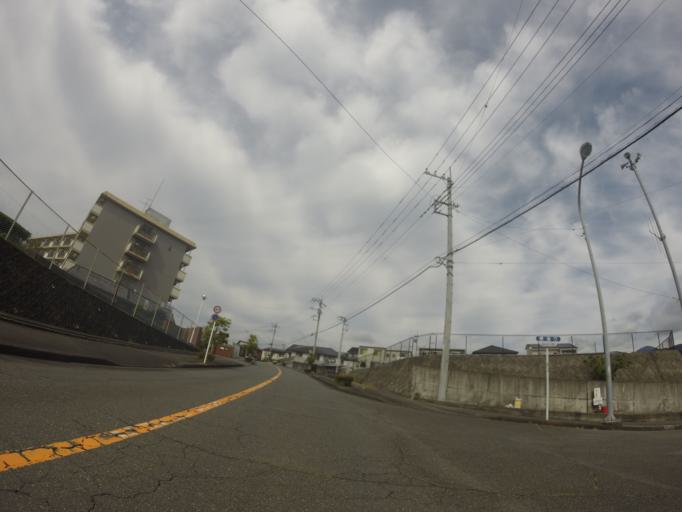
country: JP
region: Shizuoka
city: Fuji
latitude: 35.1819
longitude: 138.7193
